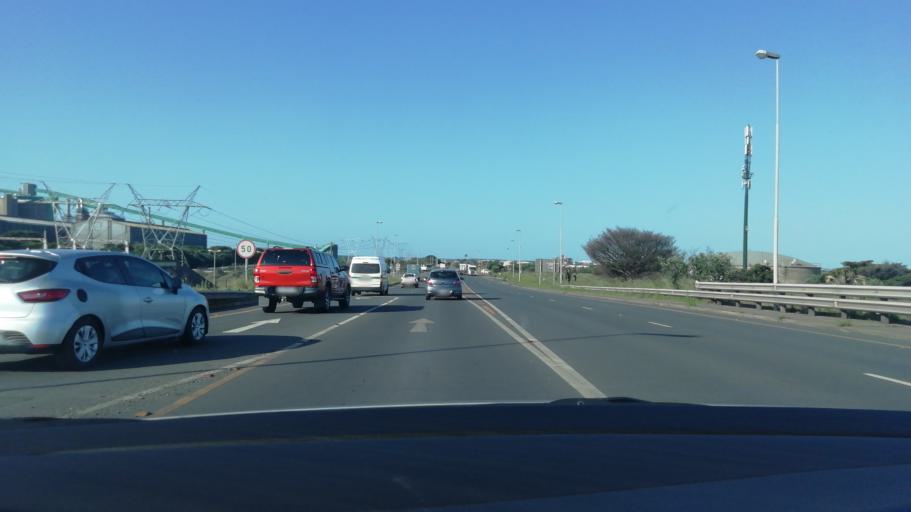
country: ZA
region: KwaZulu-Natal
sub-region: uThungulu District Municipality
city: Richards Bay
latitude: -28.7703
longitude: 32.0344
